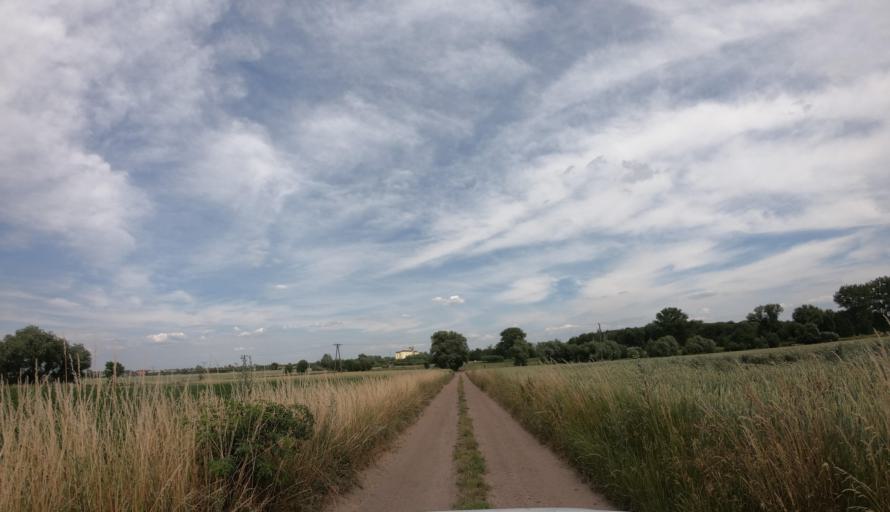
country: PL
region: West Pomeranian Voivodeship
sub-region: Powiat pyrzycki
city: Pyrzyce
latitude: 53.1386
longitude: 14.8675
